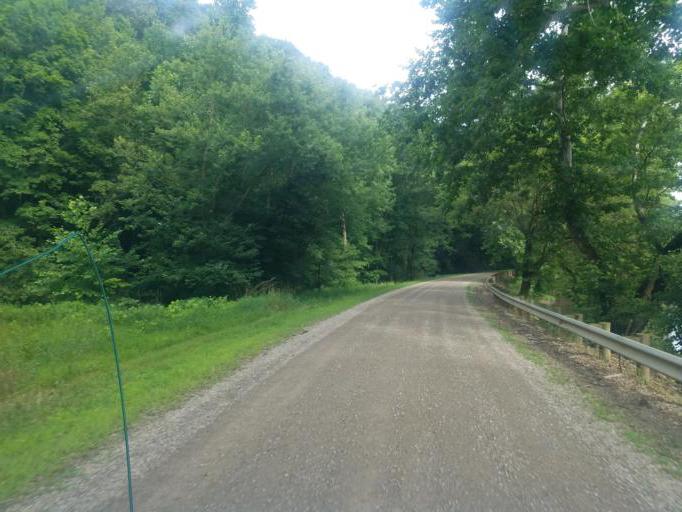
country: US
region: Ohio
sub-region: Knox County
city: Oak Hill
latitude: 40.3989
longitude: -82.1616
